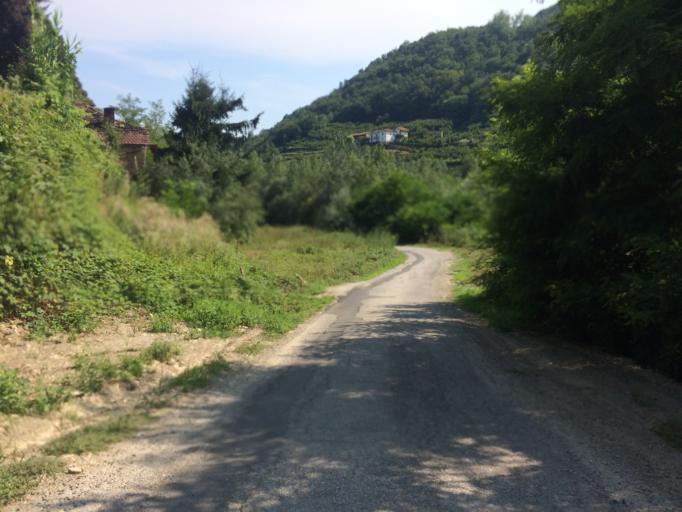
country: IT
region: Piedmont
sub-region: Provincia di Cuneo
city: Cortemilia
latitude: 44.5715
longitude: 8.2023
